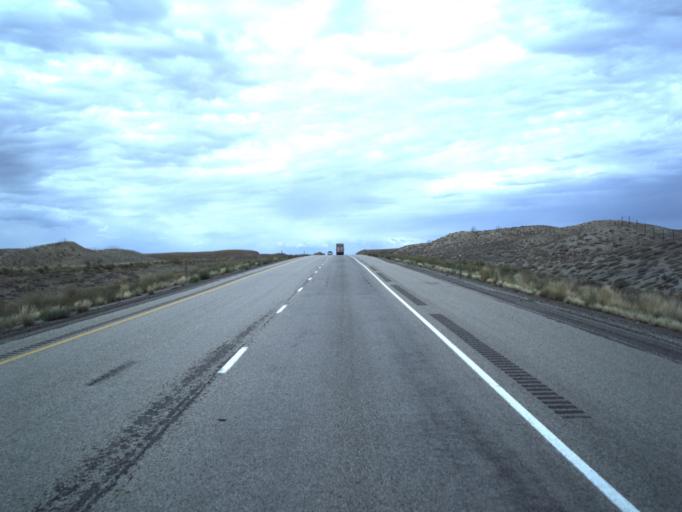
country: US
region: Utah
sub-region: Grand County
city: Moab
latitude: 39.0170
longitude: -109.3017
